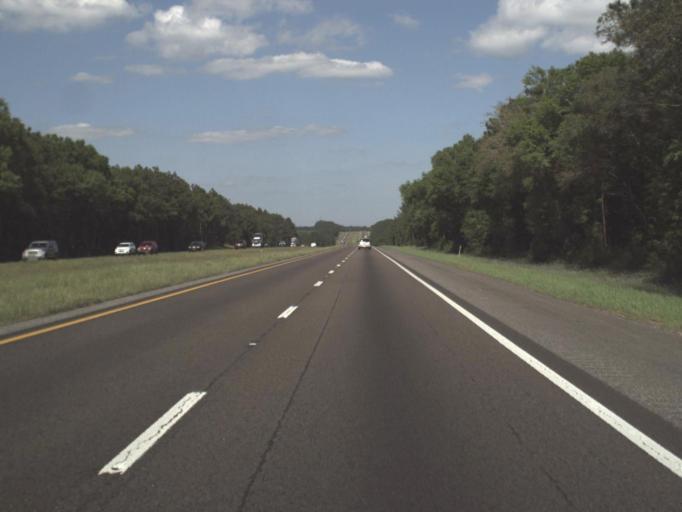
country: US
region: Florida
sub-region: Santa Rosa County
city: East Milton
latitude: 30.6588
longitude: -86.8720
